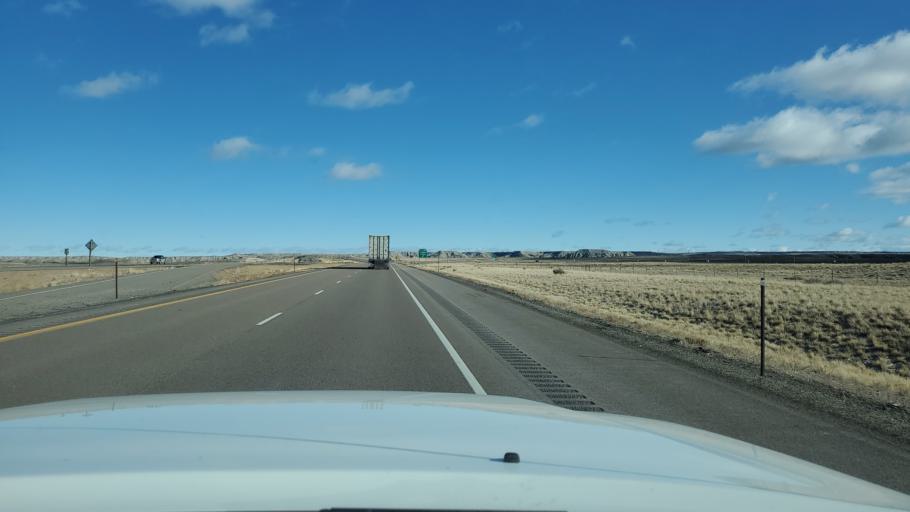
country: US
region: Wyoming
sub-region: Uinta County
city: Lyman
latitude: 41.3901
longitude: -110.1948
